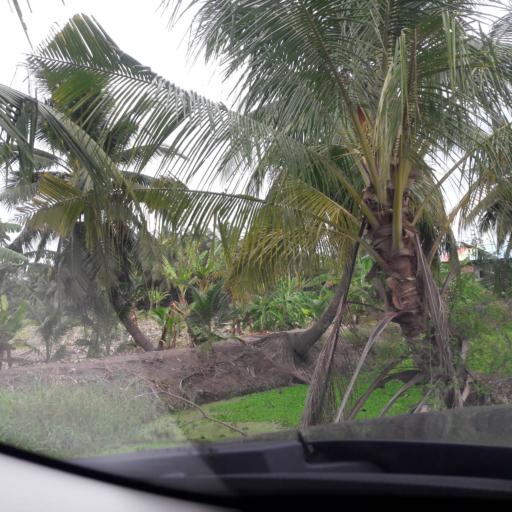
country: TH
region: Ratchaburi
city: Damnoen Saduak
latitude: 13.5741
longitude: 99.9406
